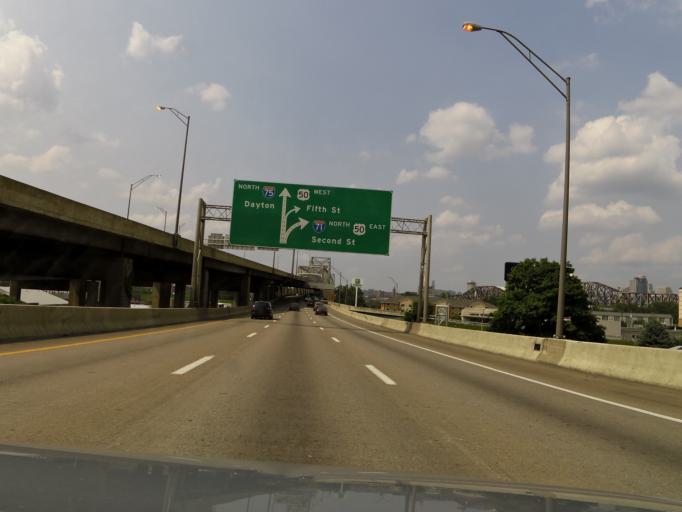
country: US
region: Kentucky
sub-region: Kenton County
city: Covington
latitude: 39.0854
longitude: -84.5226
